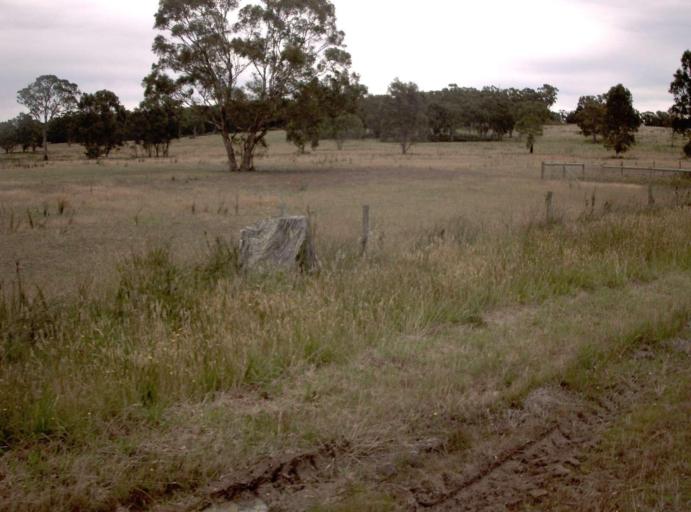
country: AU
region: Victoria
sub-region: East Gippsland
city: Bairnsdale
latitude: -37.9398
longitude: 147.5287
